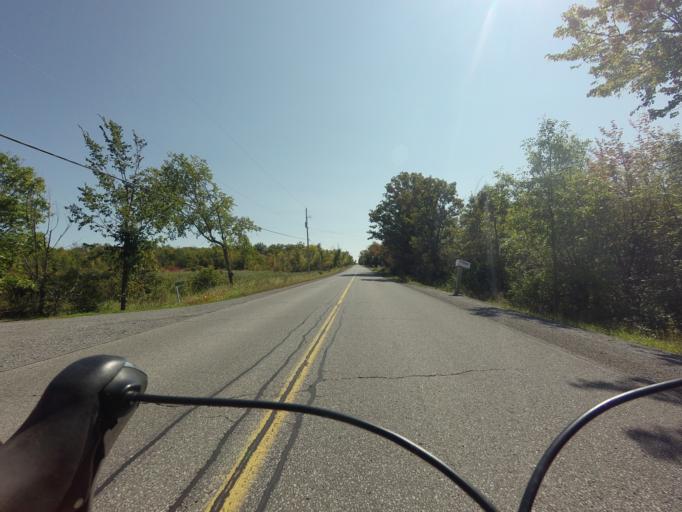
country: CA
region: Ontario
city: Bells Corners
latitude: 45.3981
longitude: -76.0162
